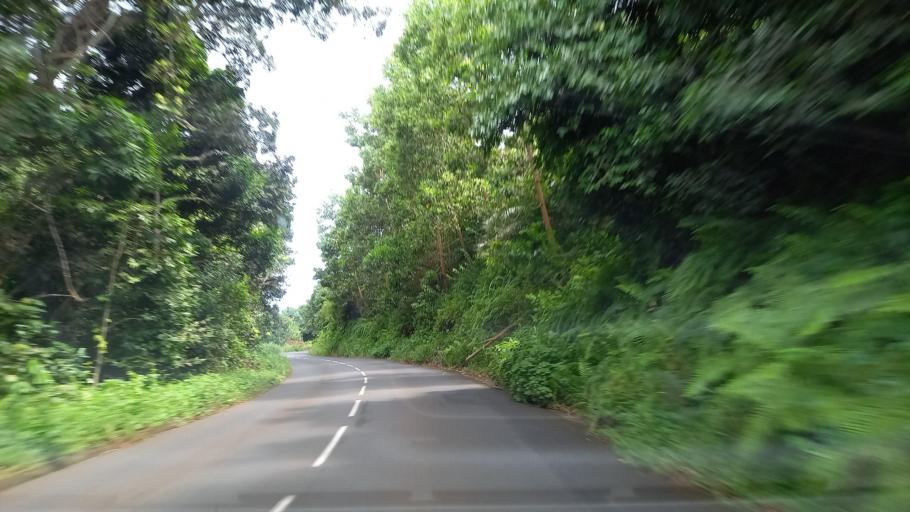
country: YT
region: Tsingoni
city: Tsingoni
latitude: -12.7882
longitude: 45.1556
